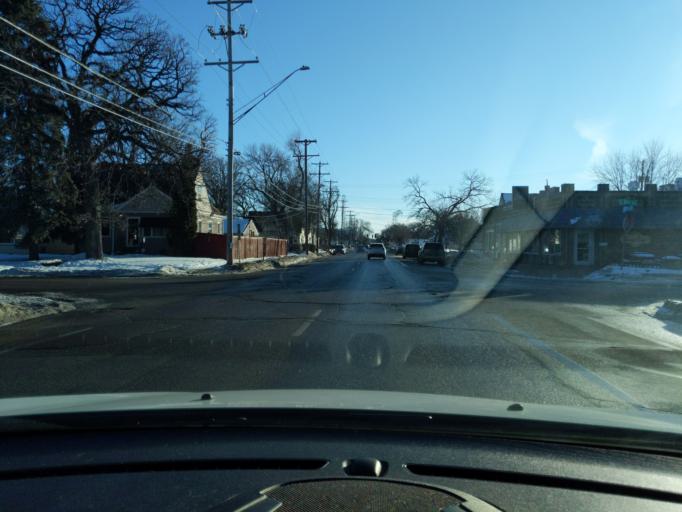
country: US
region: Minnesota
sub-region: Hennepin County
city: Minneapolis
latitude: 44.9269
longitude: -93.2273
